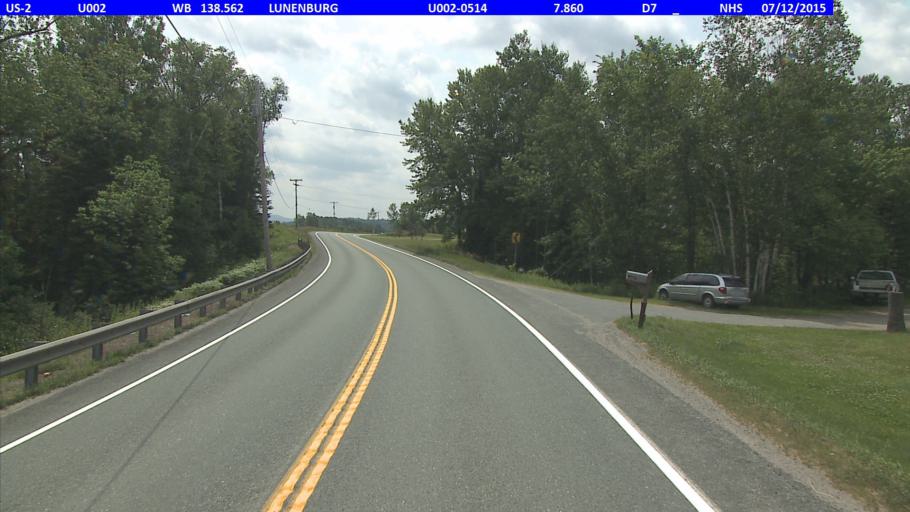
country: US
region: New Hampshire
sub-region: Coos County
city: Lancaster
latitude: 44.4845
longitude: -71.6328
